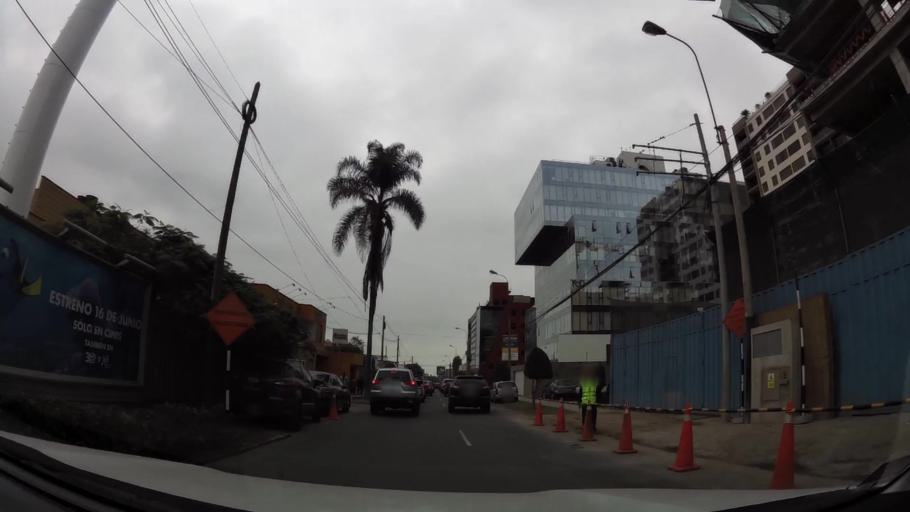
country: PE
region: Lima
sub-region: Lima
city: La Molina
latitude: -12.1040
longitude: -76.9727
